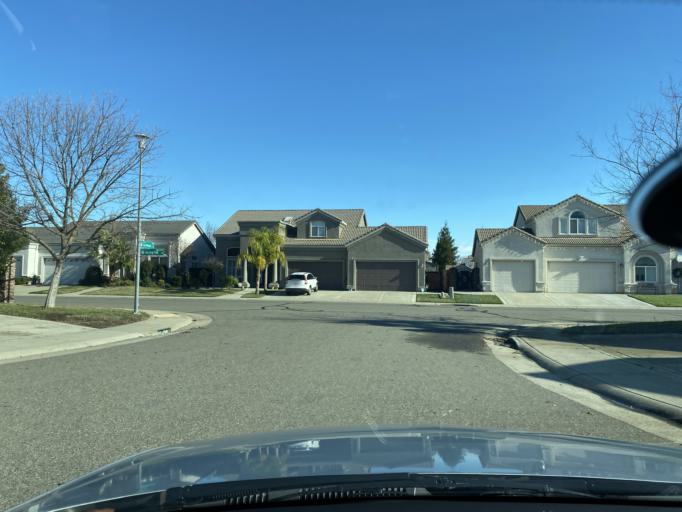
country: US
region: California
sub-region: Sacramento County
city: Elk Grove
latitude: 38.4360
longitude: -121.3875
